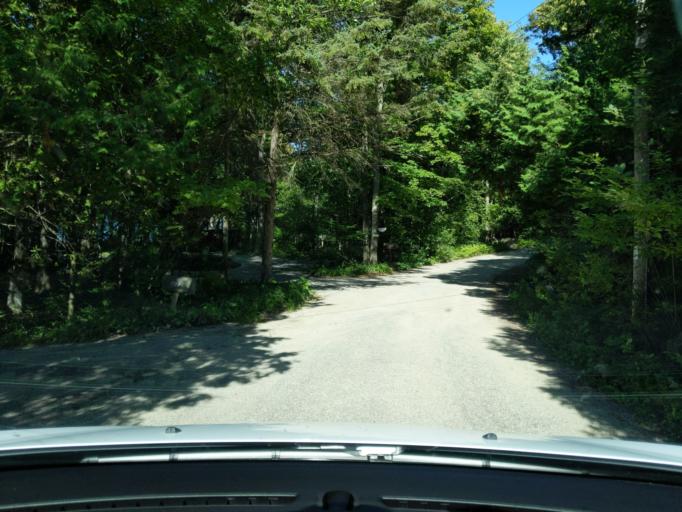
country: US
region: Wisconsin
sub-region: Door County
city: Sturgeon Bay
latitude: 45.1912
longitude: -87.1462
